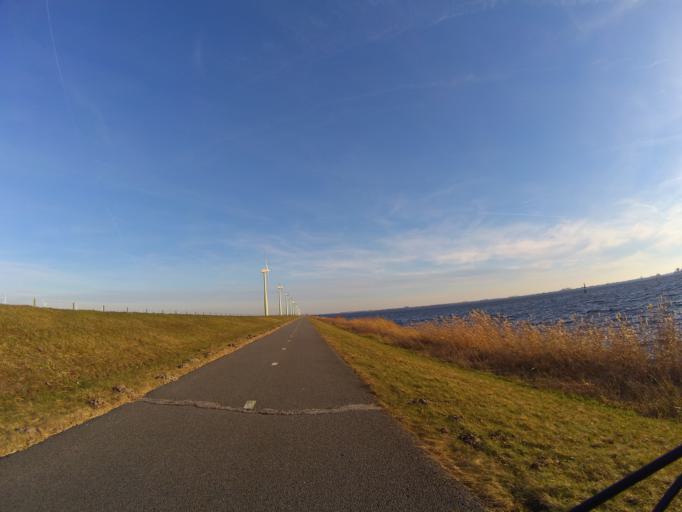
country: NL
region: Utrecht
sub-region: Gemeente Bunschoten
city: Spakenburg
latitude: 52.2908
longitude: 5.3400
